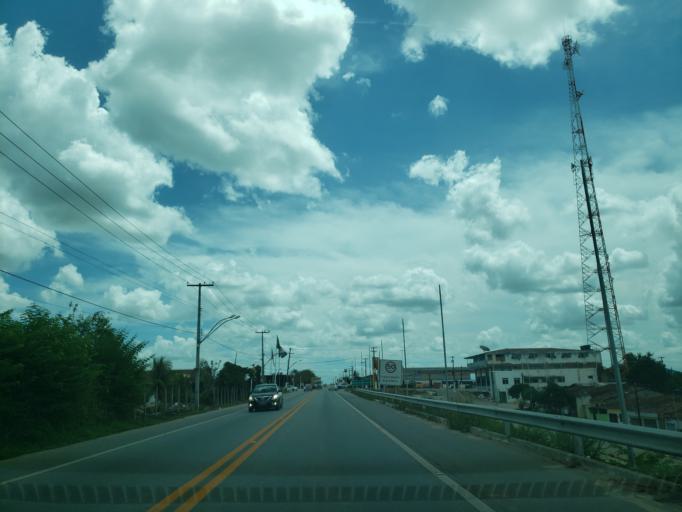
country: BR
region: Alagoas
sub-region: Uniao Dos Palmares
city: Uniao dos Palmares
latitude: -9.1655
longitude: -36.0203
